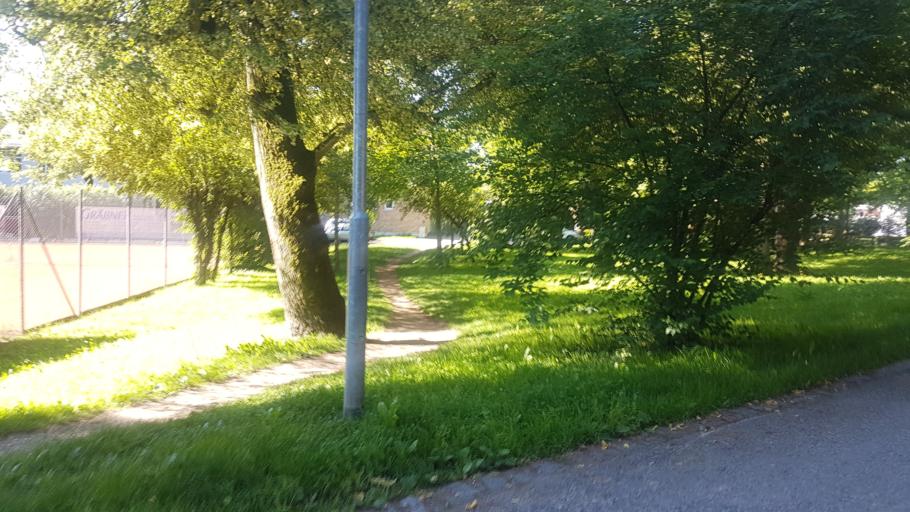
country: DE
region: Bavaria
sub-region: Upper Bavaria
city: Neuburg an der Donau
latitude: 48.7392
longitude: 11.1868
